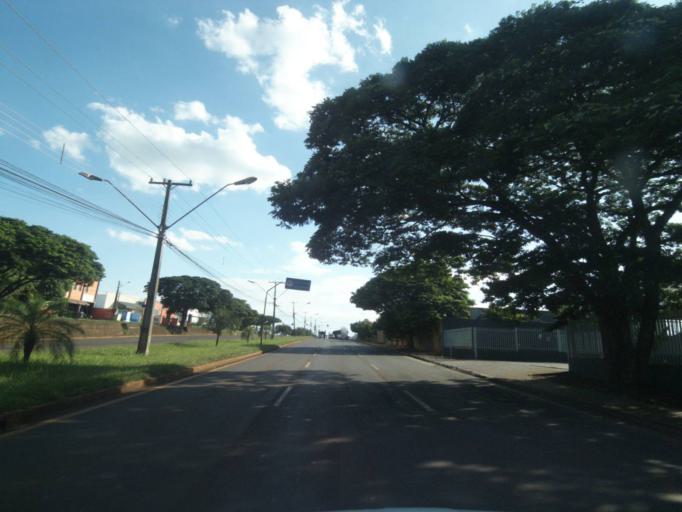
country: BR
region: Parana
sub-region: Londrina
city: Londrina
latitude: -23.3557
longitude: -51.1497
